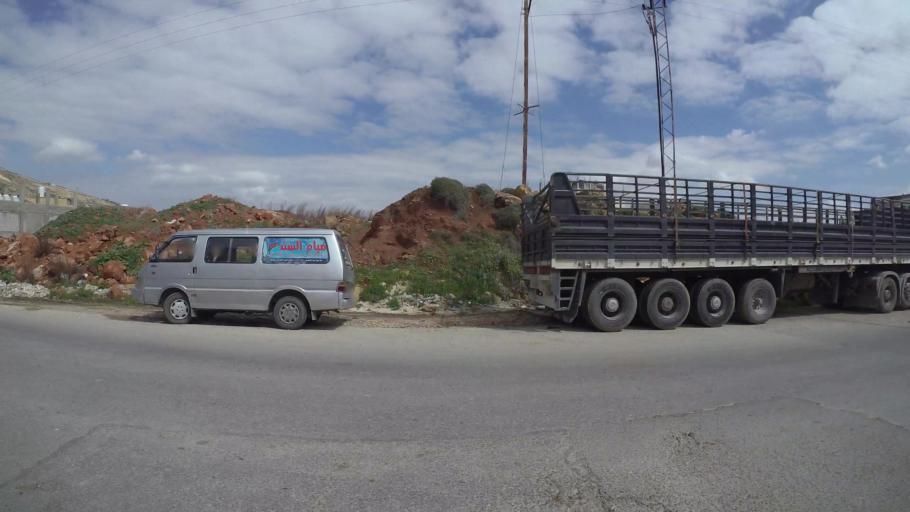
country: JO
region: Amman
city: Al Jubayhah
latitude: 32.0606
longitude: 35.8105
